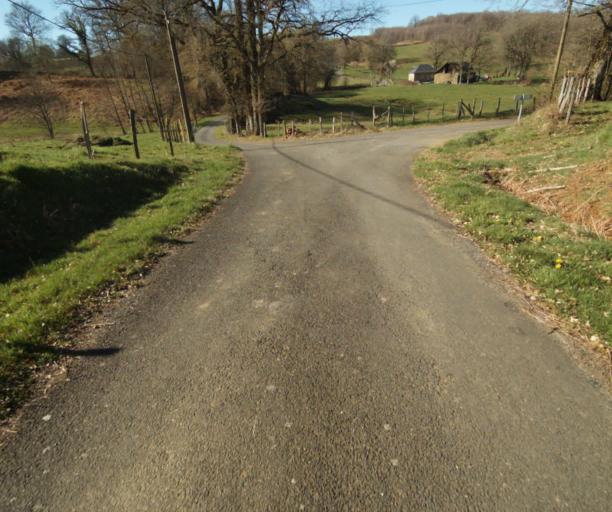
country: FR
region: Limousin
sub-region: Departement de la Correze
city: Chamboulive
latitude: 45.3995
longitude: 1.7019
